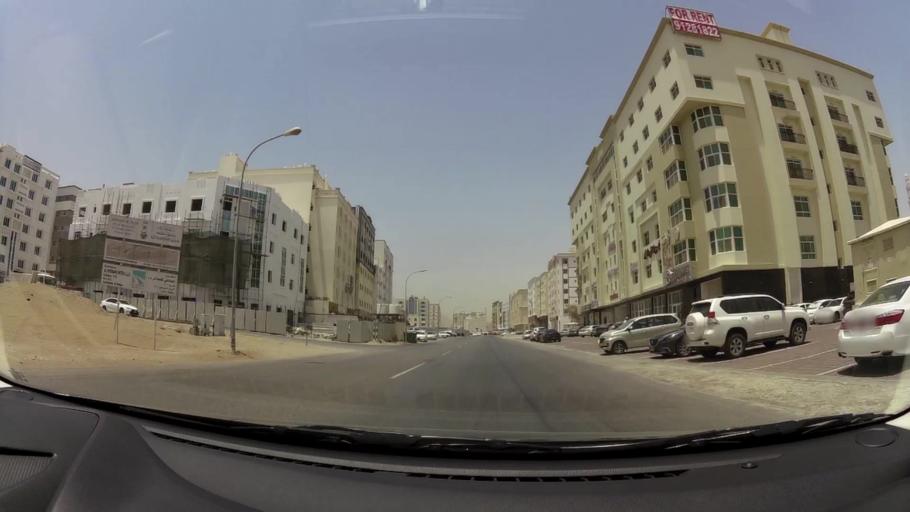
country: OM
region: Muhafazat Masqat
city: Bawshar
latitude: 23.5779
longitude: 58.4190
